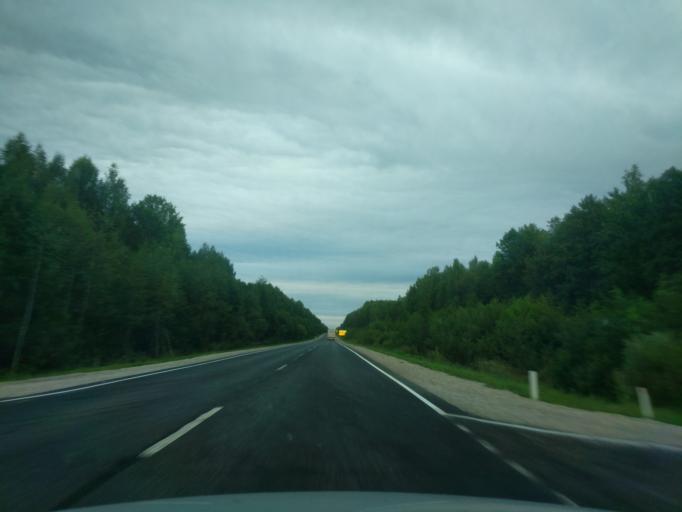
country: RU
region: Kostroma
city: Ponazyrevo
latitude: 58.3234
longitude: 46.5222
